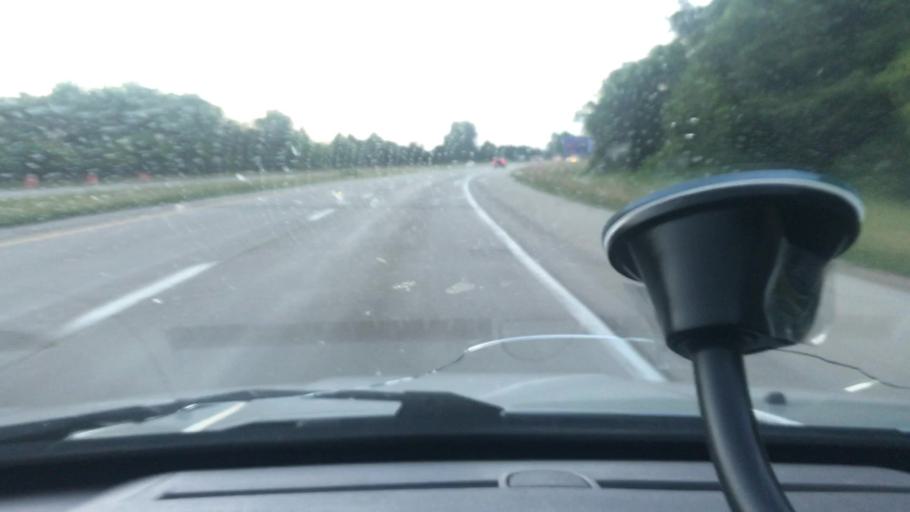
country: US
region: Illinois
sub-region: Peoria County
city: Bellevue
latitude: 40.7498
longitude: -89.6701
